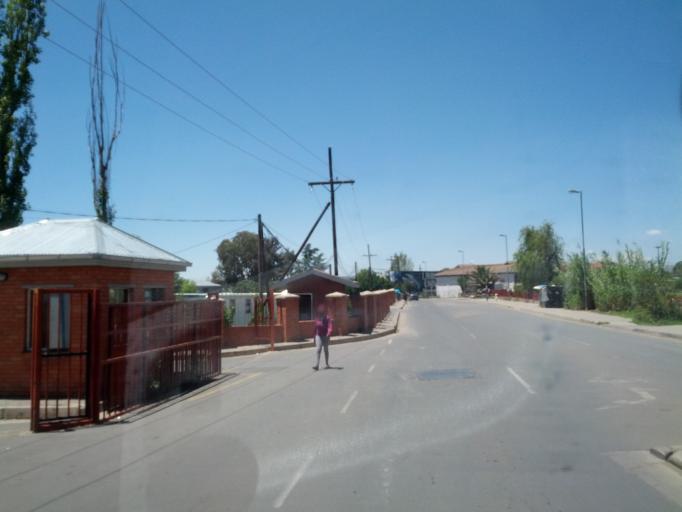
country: LS
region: Maseru
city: Maseru
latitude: -29.3069
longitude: 27.4855
